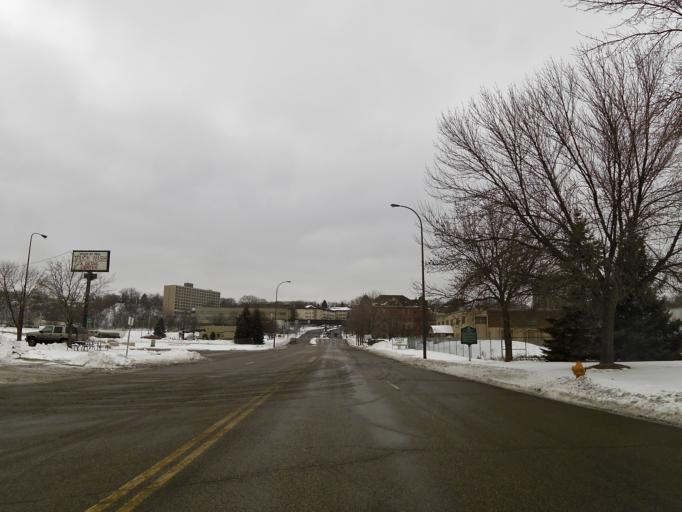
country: US
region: Minnesota
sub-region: Dakota County
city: South Saint Paul
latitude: 44.8941
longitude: -93.0316
